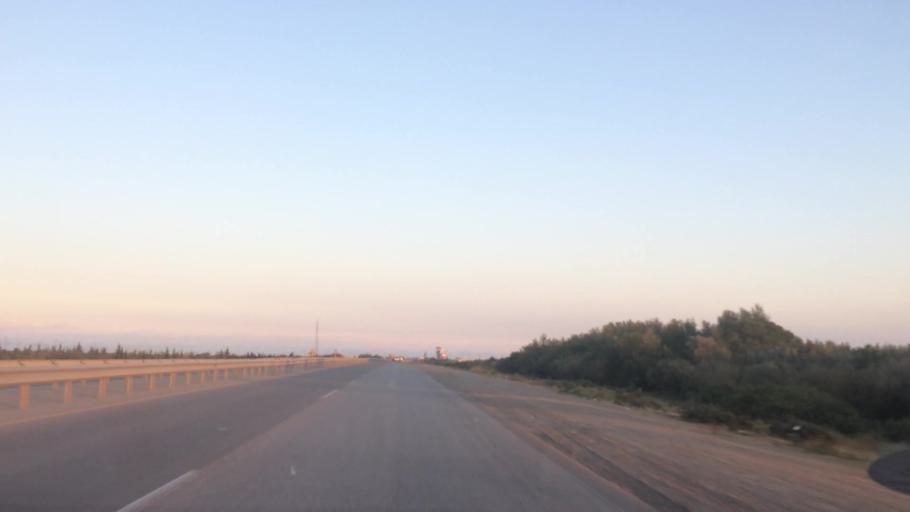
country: AZ
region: Baki
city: Qobustan
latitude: 39.9514
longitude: 49.3203
